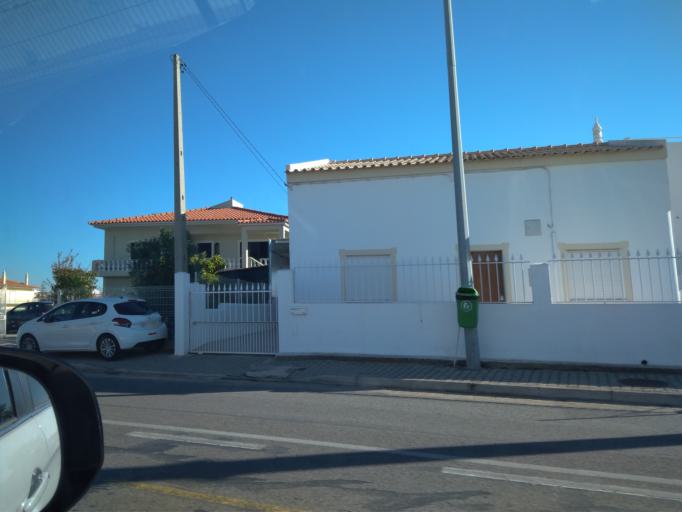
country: PT
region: Faro
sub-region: Faro
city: Faro
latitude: 37.0243
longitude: -7.9699
